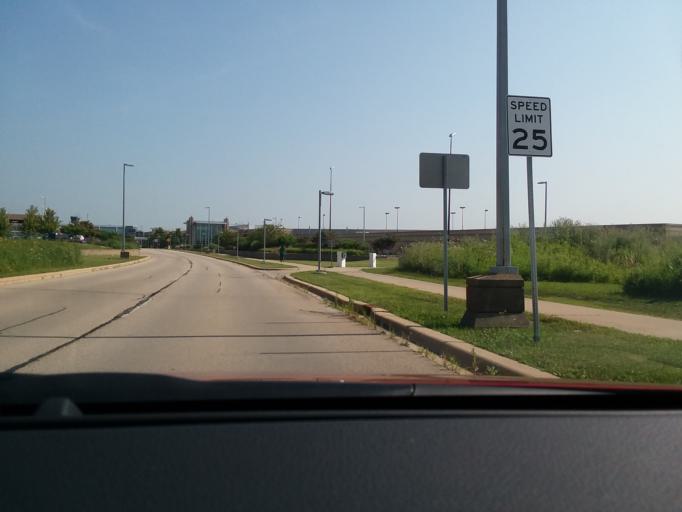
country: US
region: Wisconsin
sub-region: Dane County
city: Maple Bluff
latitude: 43.1330
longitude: -89.3468
